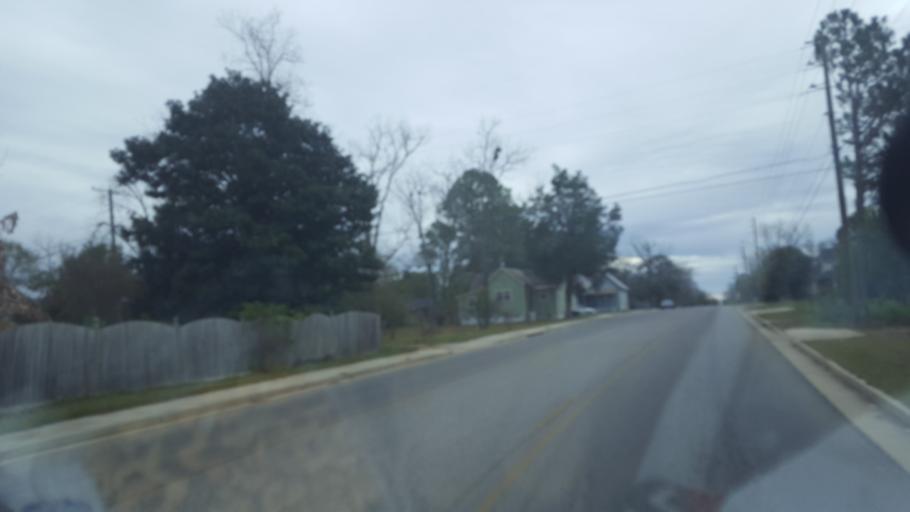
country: US
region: Georgia
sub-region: Ben Hill County
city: Fitzgerald
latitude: 31.7225
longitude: -83.2600
